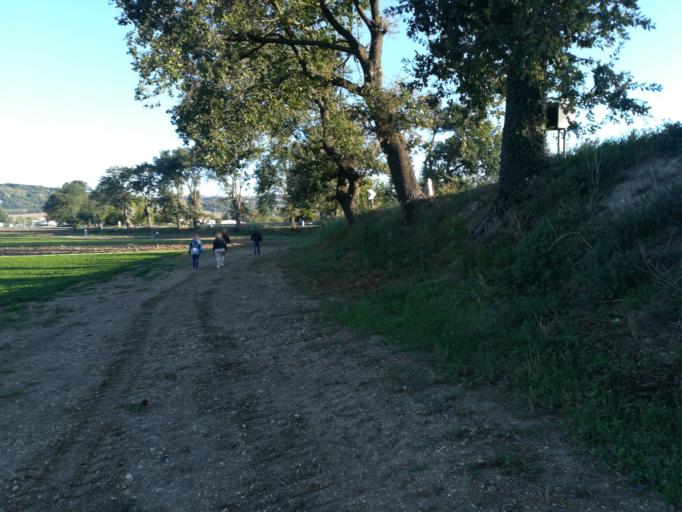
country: IT
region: The Marches
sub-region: Provincia di Macerata
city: Villa Potenza
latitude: 43.3307
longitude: 13.4164
